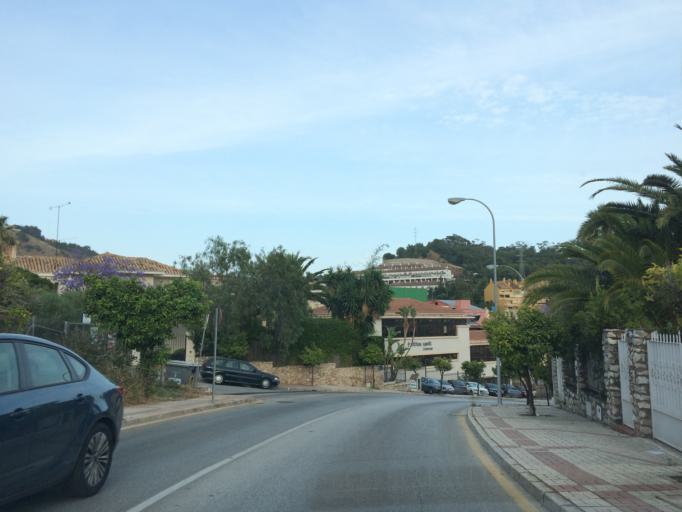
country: ES
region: Andalusia
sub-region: Provincia de Malaga
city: Malaga
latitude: 36.7336
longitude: -4.3984
